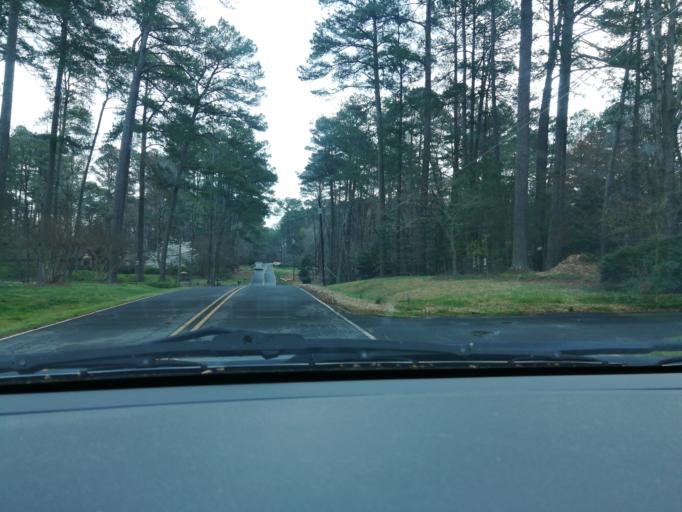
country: US
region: North Carolina
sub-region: Durham County
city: Durham
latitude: 36.0668
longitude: -78.9685
